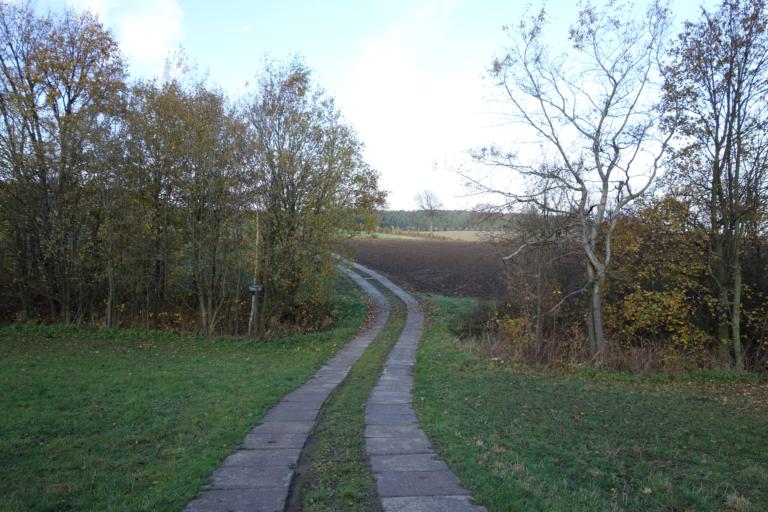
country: DE
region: Saxony
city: Rechenberg-Bienenmuhle
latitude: 50.7239
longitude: 13.4960
